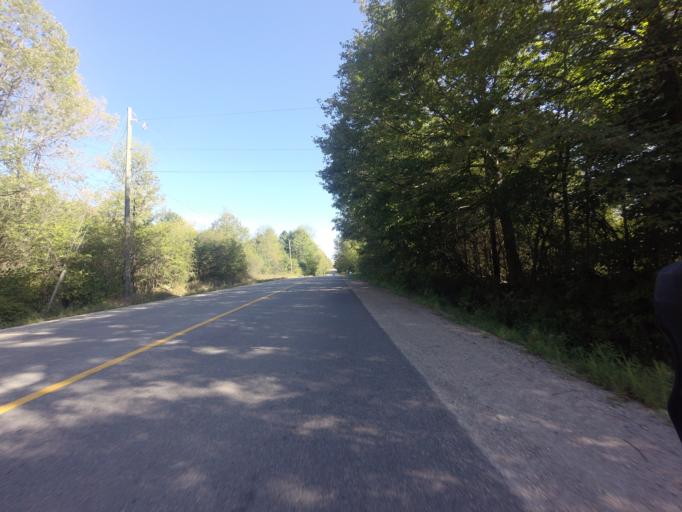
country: CA
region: Ontario
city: Perth
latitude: 44.9070
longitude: -76.3387
